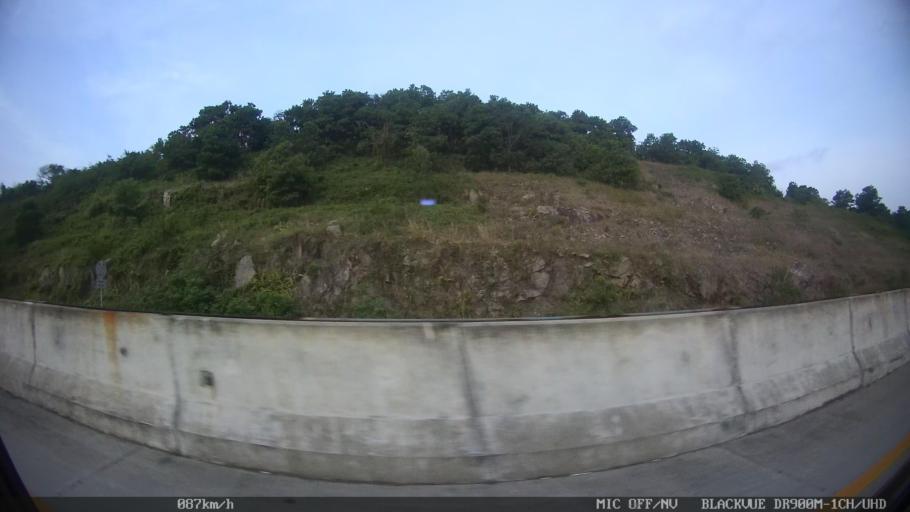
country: ID
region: Lampung
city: Penengahan
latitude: -5.8529
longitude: 105.7286
